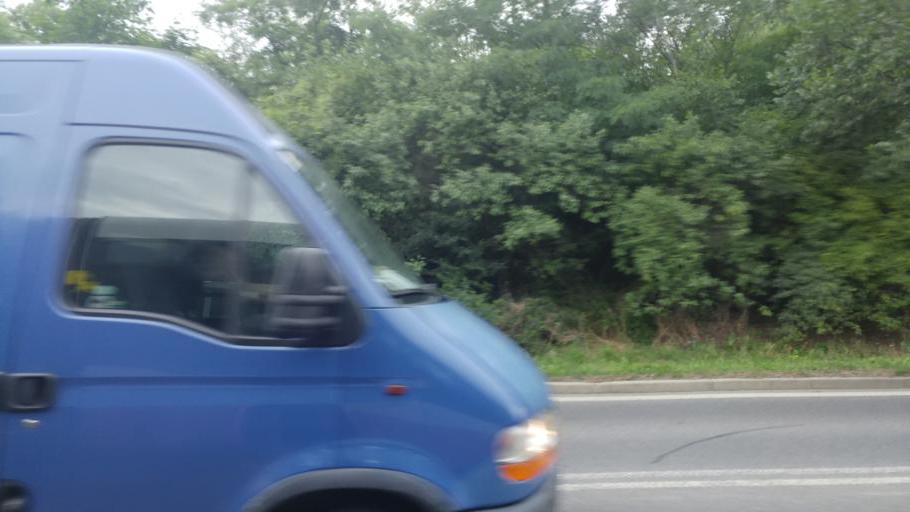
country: CZ
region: Central Bohemia
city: Roztoky
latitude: 50.1281
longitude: 14.3903
